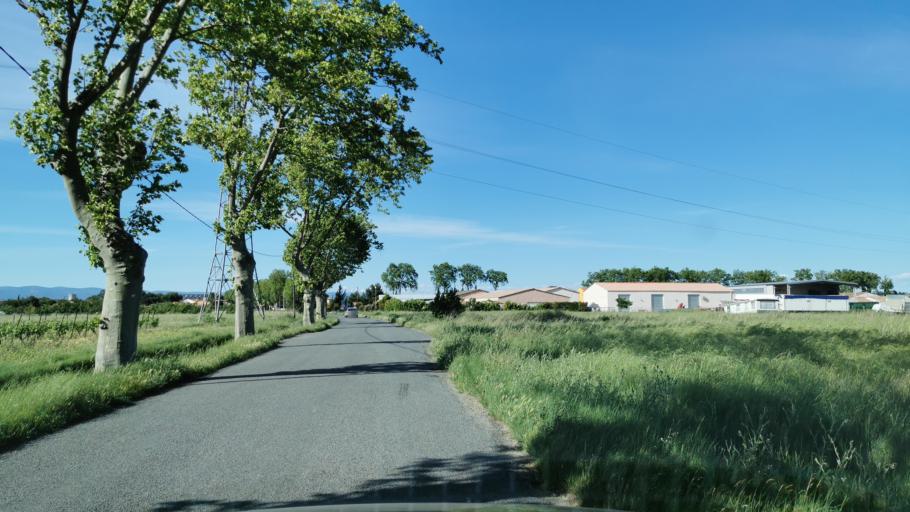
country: FR
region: Languedoc-Roussillon
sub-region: Departement de l'Aude
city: Canet
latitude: 43.2164
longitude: 2.8453
